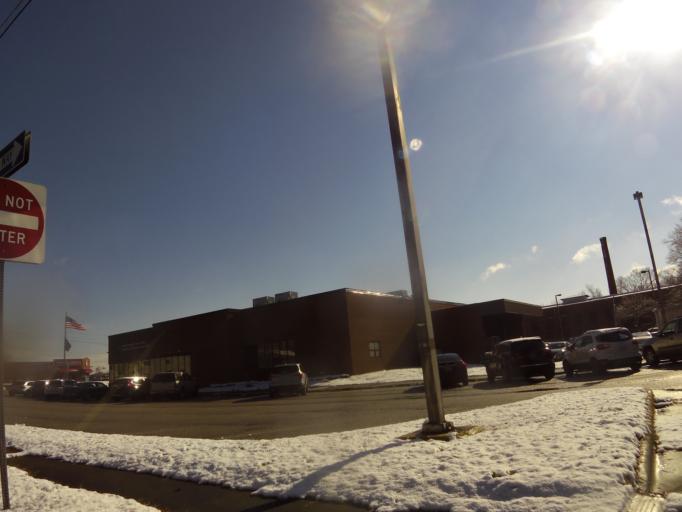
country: US
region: North Carolina
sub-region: Wilson County
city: Wilson
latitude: 35.7217
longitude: -77.9173
